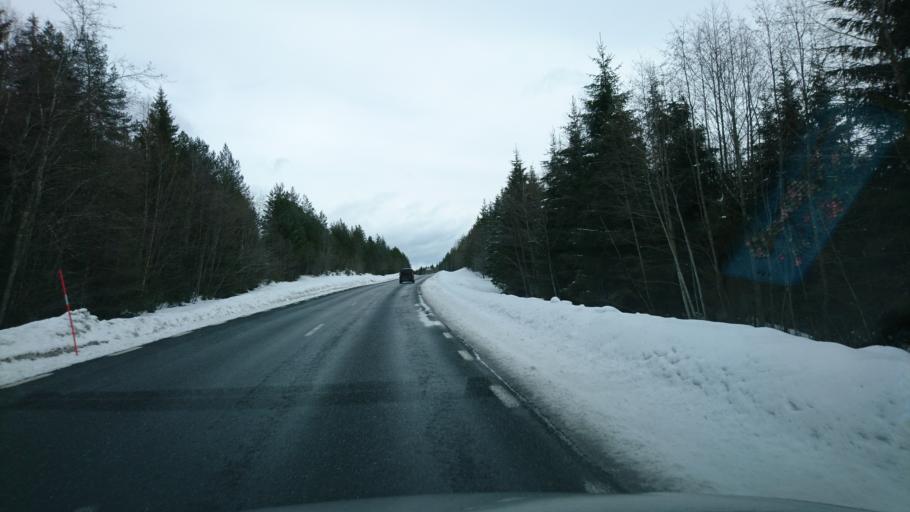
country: SE
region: Vaesternorrland
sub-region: Solleftea Kommun
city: Solleftea
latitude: 63.0544
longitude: 17.0422
